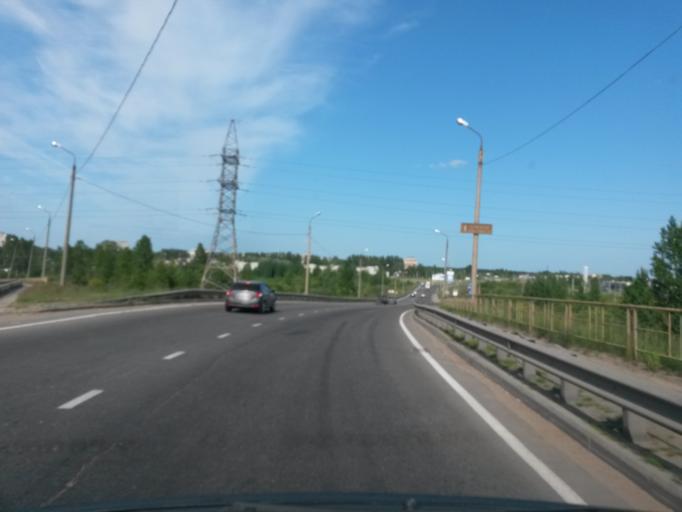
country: RU
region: Jaroslavl
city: Yaroslavl
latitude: 57.6685
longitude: 39.7678
